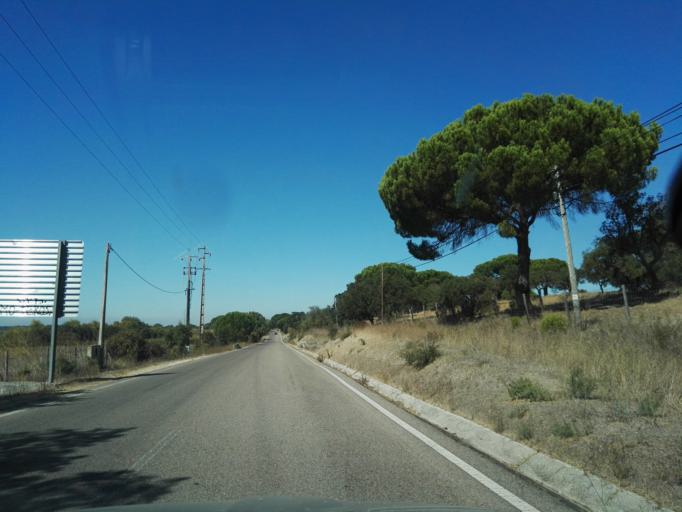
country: PT
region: Santarem
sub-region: Benavente
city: Poceirao
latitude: 38.8511
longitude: -8.7206
